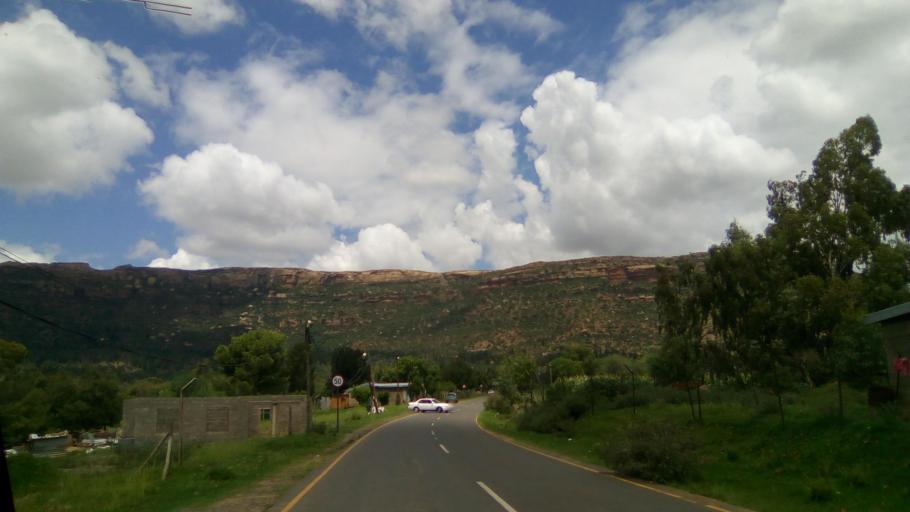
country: LS
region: Maseru
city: Nako
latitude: -29.6238
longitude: 27.5033
